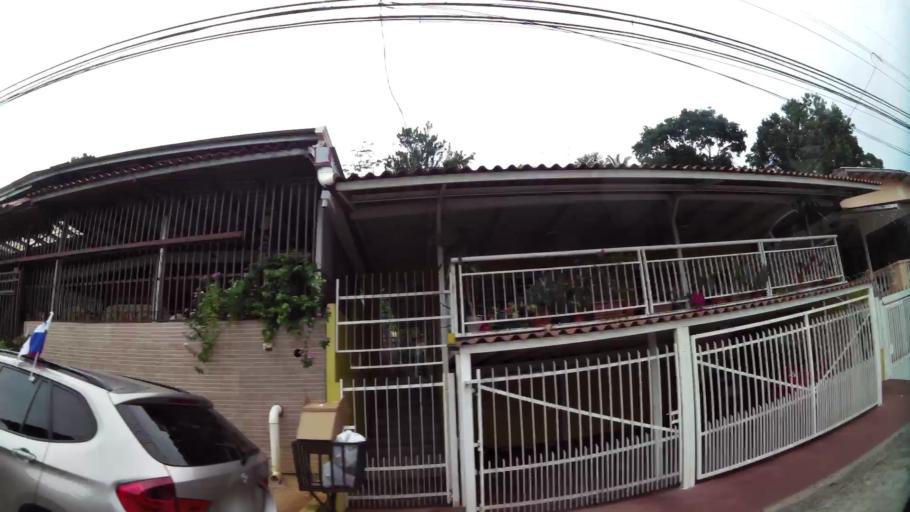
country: PA
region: Panama
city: Panama
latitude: 9.0161
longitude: -79.5292
